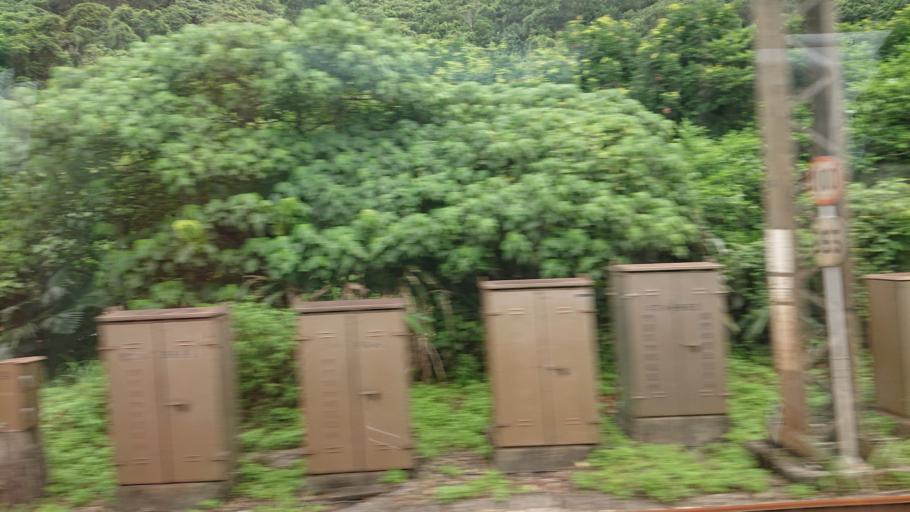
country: TW
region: Taiwan
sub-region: Yilan
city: Yilan
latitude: 24.9142
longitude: 121.8784
